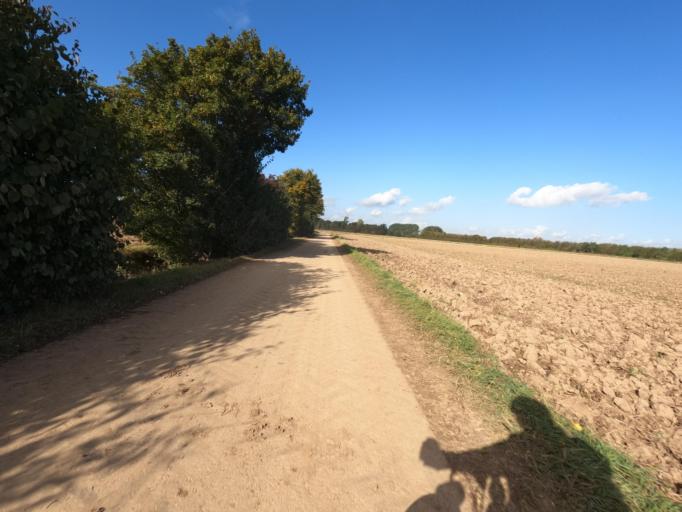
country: DE
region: North Rhine-Westphalia
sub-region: Regierungsbezirk Koln
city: Inden
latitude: 50.8697
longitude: 6.4096
